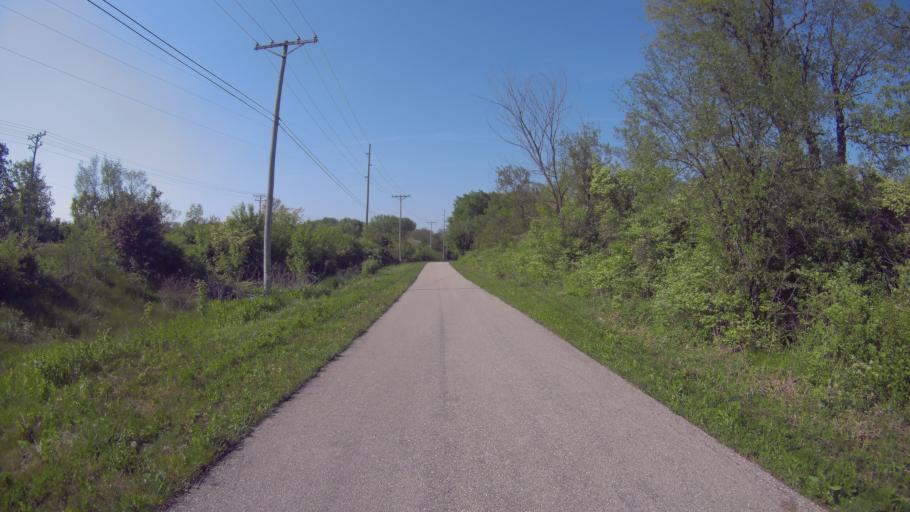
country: US
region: Wisconsin
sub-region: Dane County
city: Shorewood Hills
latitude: 43.0217
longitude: -89.4612
